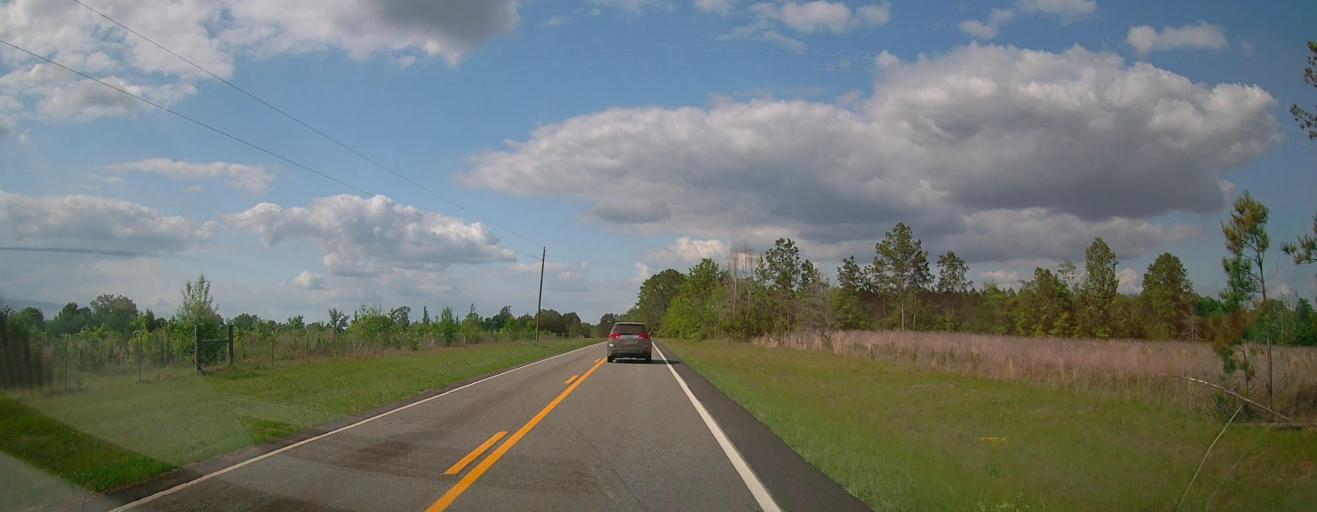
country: US
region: Georgia
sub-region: Laurens County
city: East Dublin
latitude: 32.6425
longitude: -82.8950
